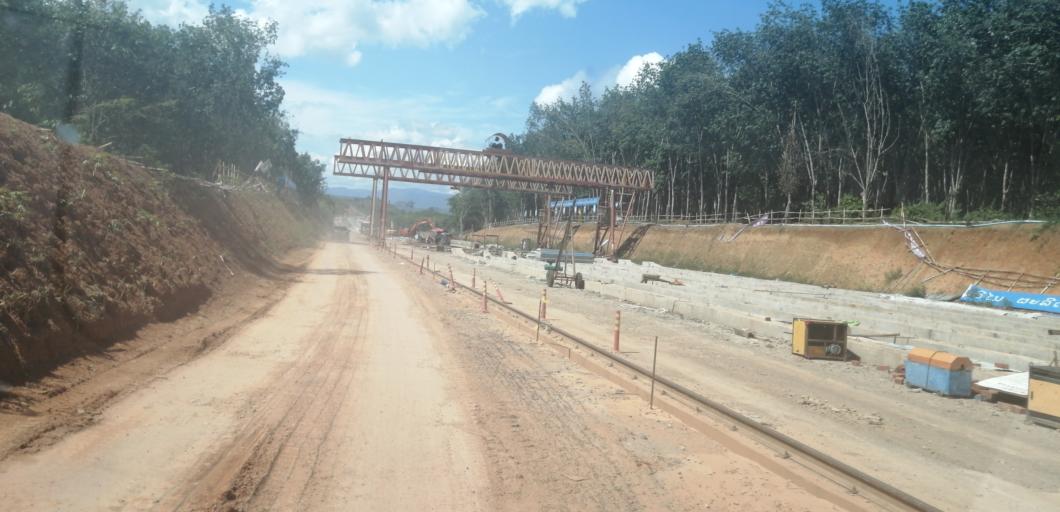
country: LA
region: Vientiane
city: Vangviang
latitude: 18.7477
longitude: 102.3841
